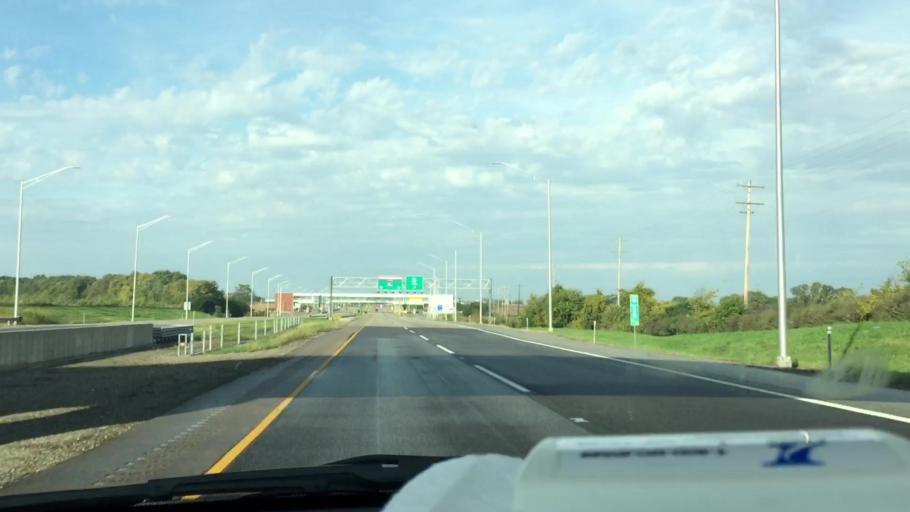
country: US
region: Illinois
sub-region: Lee County
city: Dixon
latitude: 41.8236
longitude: -89.4200
